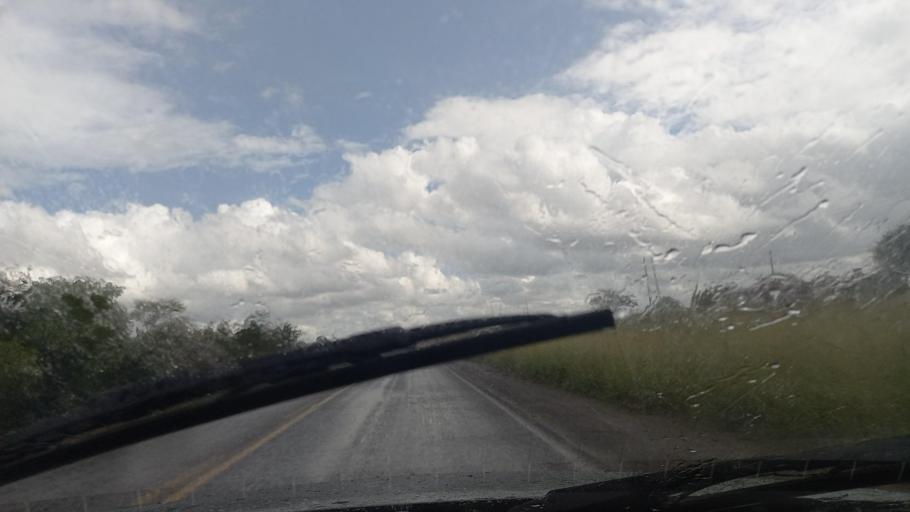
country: BR
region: Pernambuco
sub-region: Lajedo
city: Lajedo
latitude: -8.5769
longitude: -36.2858
